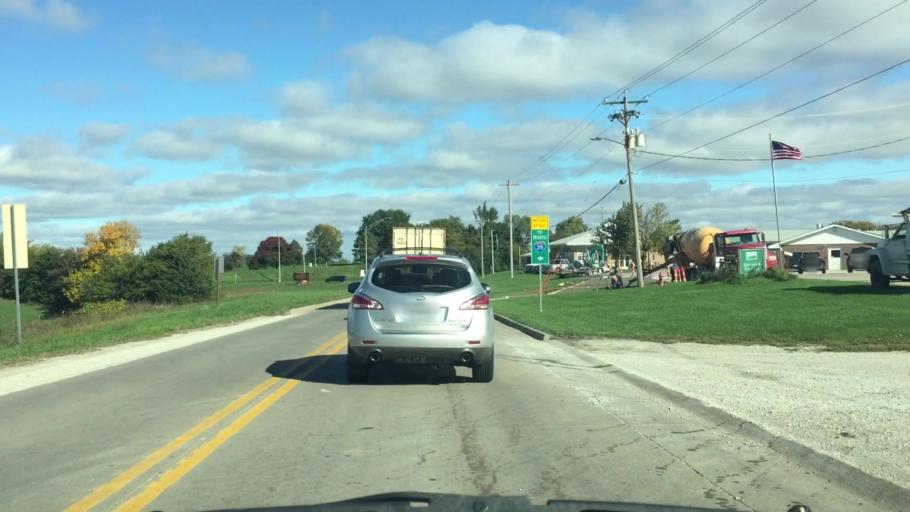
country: US
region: Iowa
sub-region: Decatur County
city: Leon
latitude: 40.7376
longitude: -93.7611
